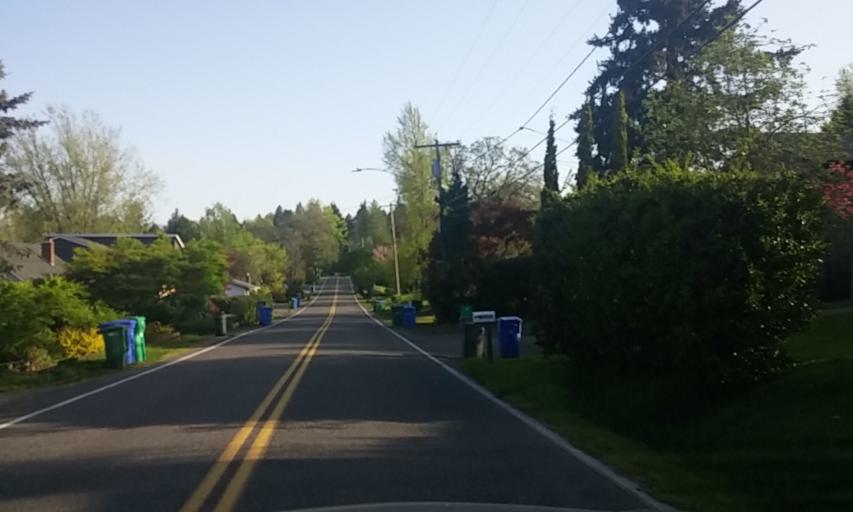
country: US
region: Oregon
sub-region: Washington County
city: Metzger
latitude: 45.4456
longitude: -122.7396
